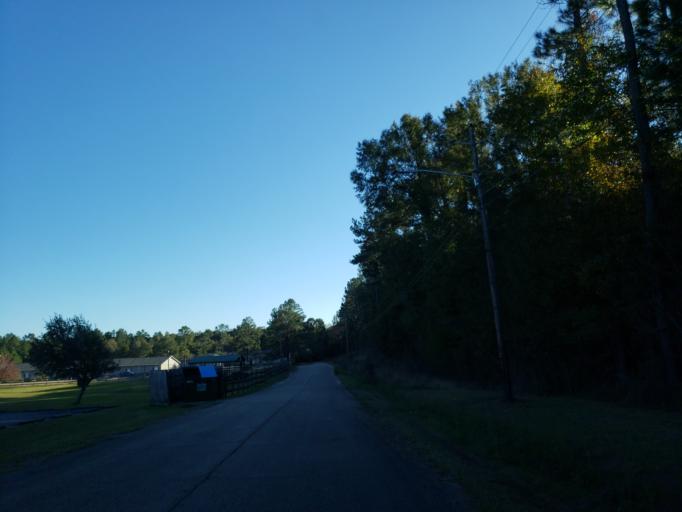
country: US
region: Mississippi
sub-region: Forrest County
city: Hattiesburg
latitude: 31.2768
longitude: -89.2841
